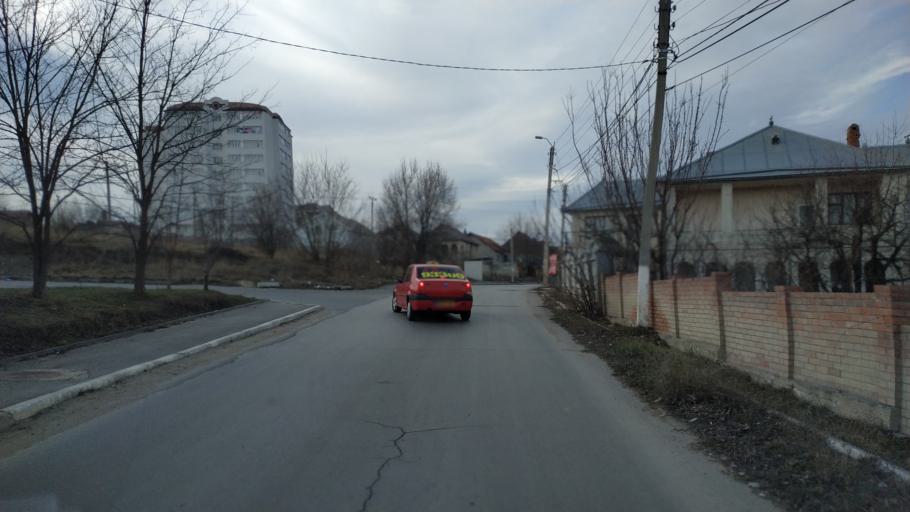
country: MD
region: Laloveni
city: Ialoveni
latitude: 46.9556
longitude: 28.7609
